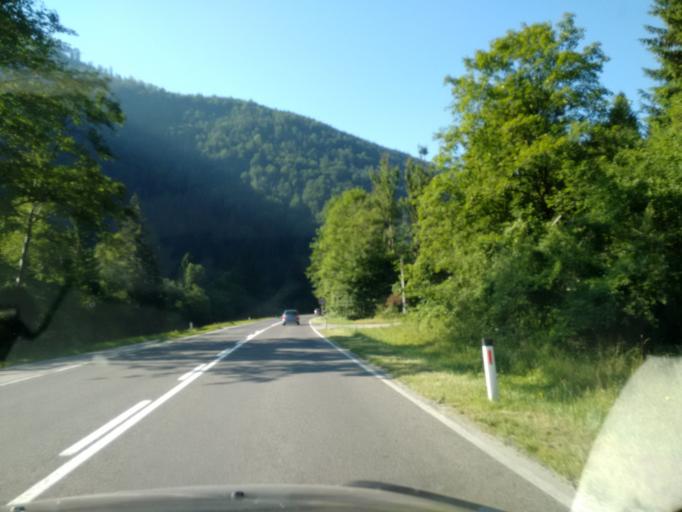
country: AT
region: Upper Austria
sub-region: Politischer Bezirk Gmunden
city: Bad Ischl
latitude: 47.7317
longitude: 13.6591
